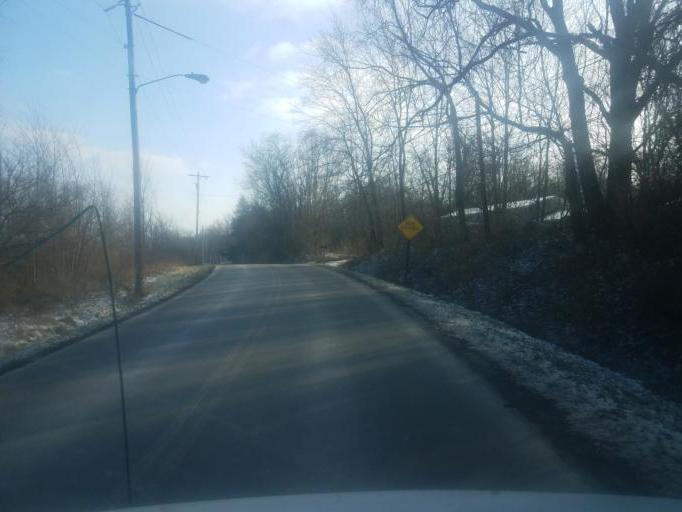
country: US
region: Ohio
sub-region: Richland County
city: Mansfield
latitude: 40.7525
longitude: -82.4999
